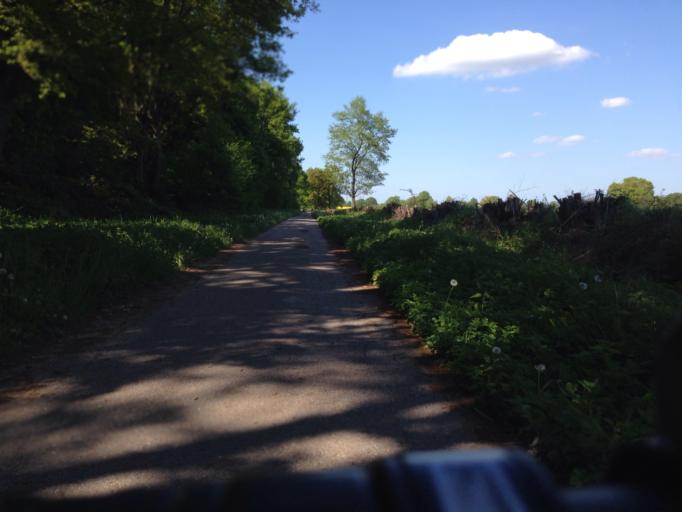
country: DE
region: Schleswig-Holstein
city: Braak
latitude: 53.6254
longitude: 10.2286
